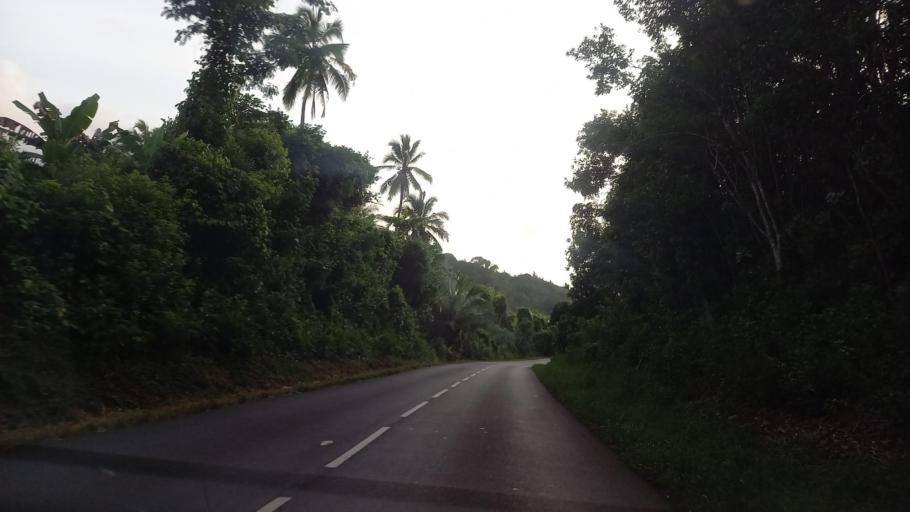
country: YT
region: M'Tsangamouji
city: M'Tsangamouji
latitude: -12.7622
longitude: 45.1091
